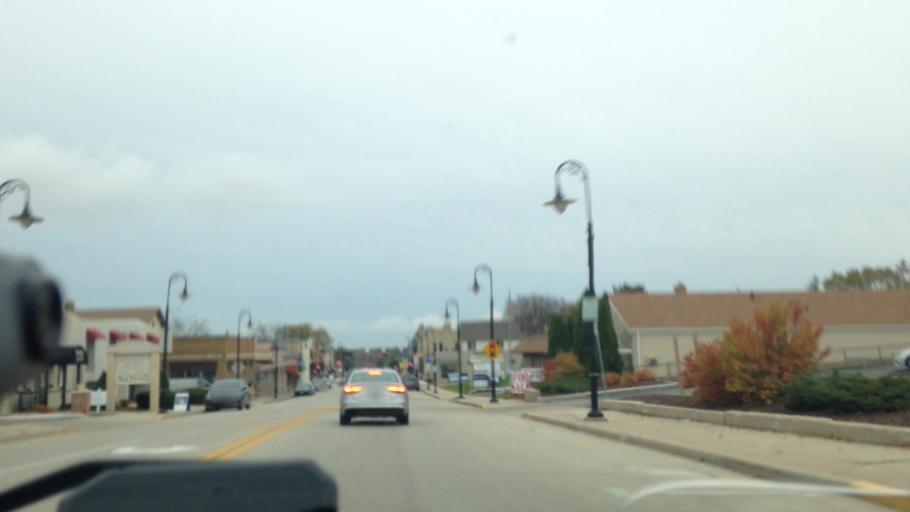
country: US
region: Wisconsin
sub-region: Waukesha County
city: Menomonee Falls
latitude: 43.1804
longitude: -88.1189
